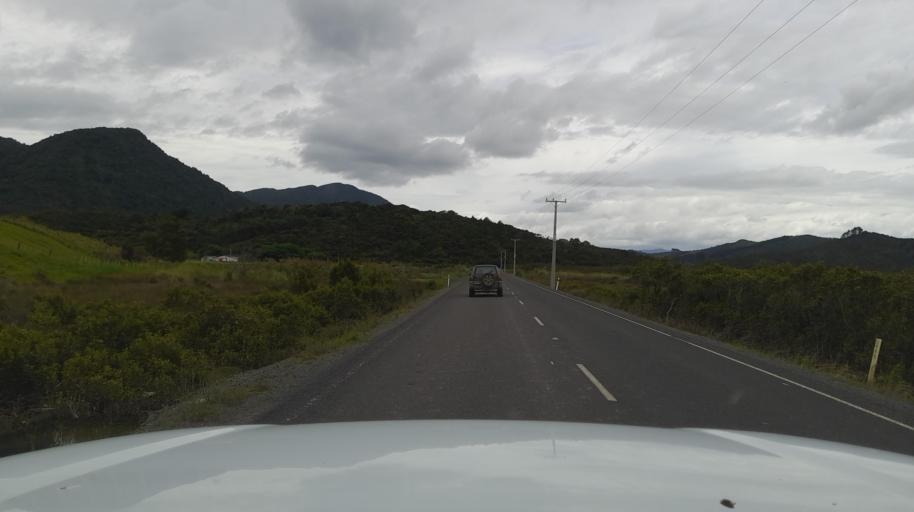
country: NZ
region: Northland
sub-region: Far North District
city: Kaitaia
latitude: -35.4054
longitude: 173.3823
